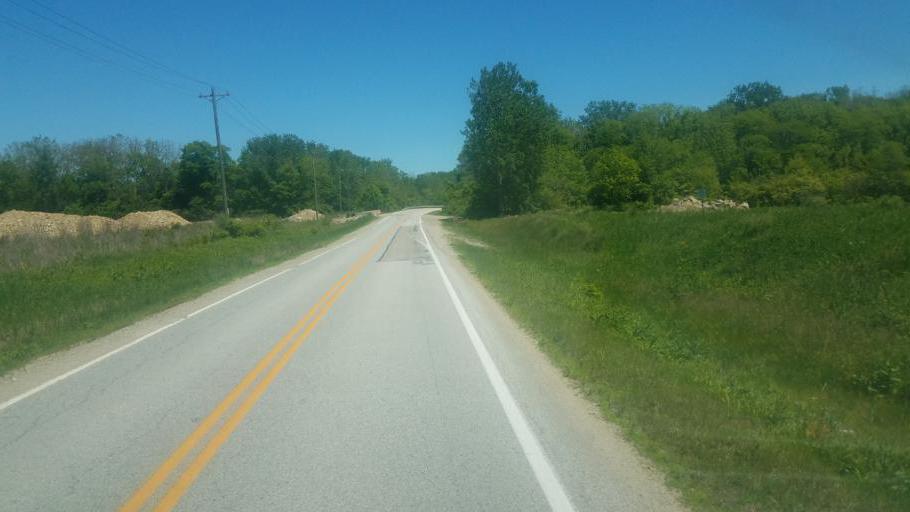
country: US
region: Ohio
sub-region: Miami County
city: Piqua
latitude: 40.2101
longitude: -84.2185
